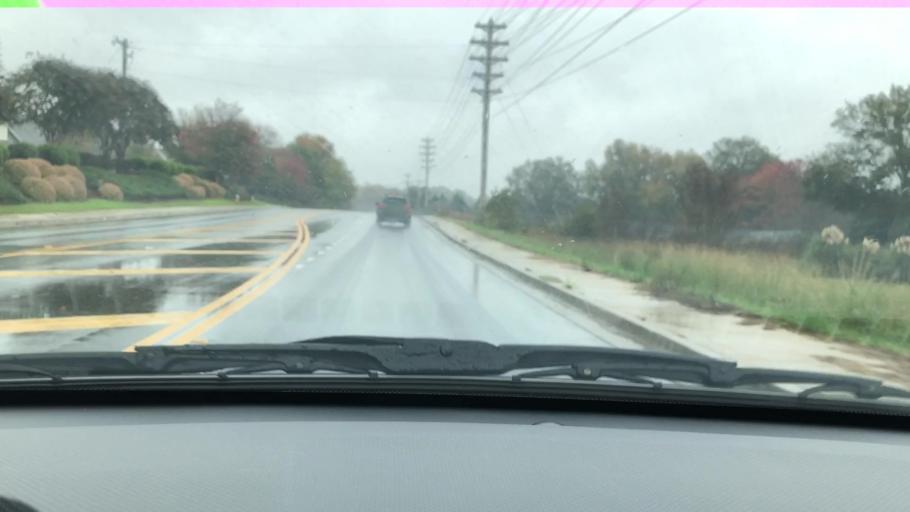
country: US
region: South Carolina
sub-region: Greenville County
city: Five Forks
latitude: 34.8320
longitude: -82.2696
